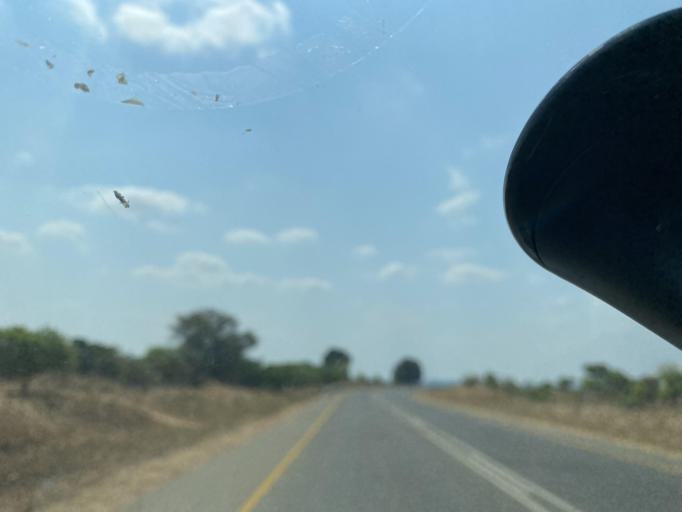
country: ZM
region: Lusaka
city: Chongwe
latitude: -15.5860
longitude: 28.7083
